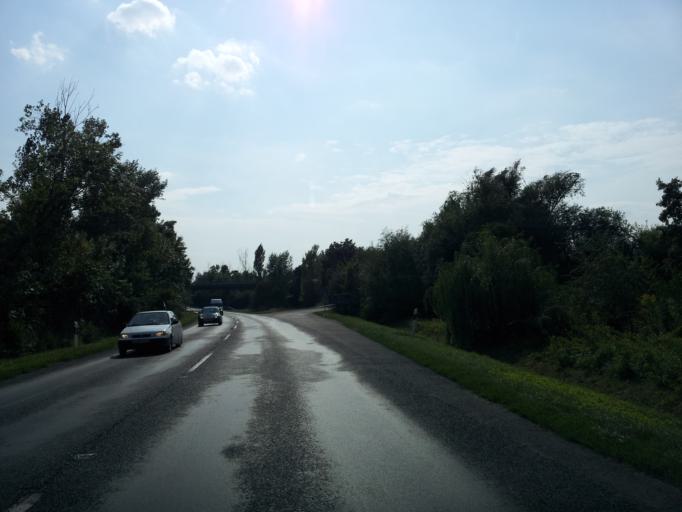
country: HU
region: Somogy
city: Balatonszabadi
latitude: 46.9351
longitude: 18.1449
